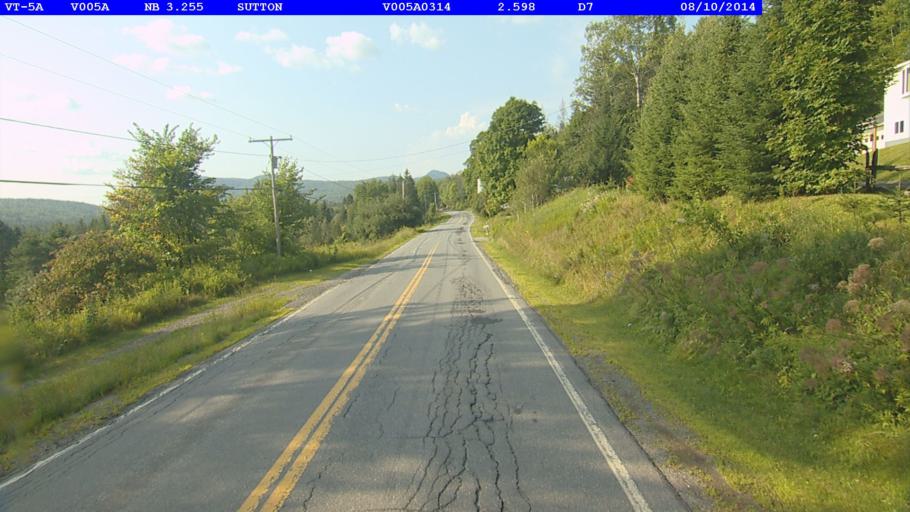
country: US
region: Vermont
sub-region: Caledonia County
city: Lyndonville
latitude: 44.6845
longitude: -71.9954
